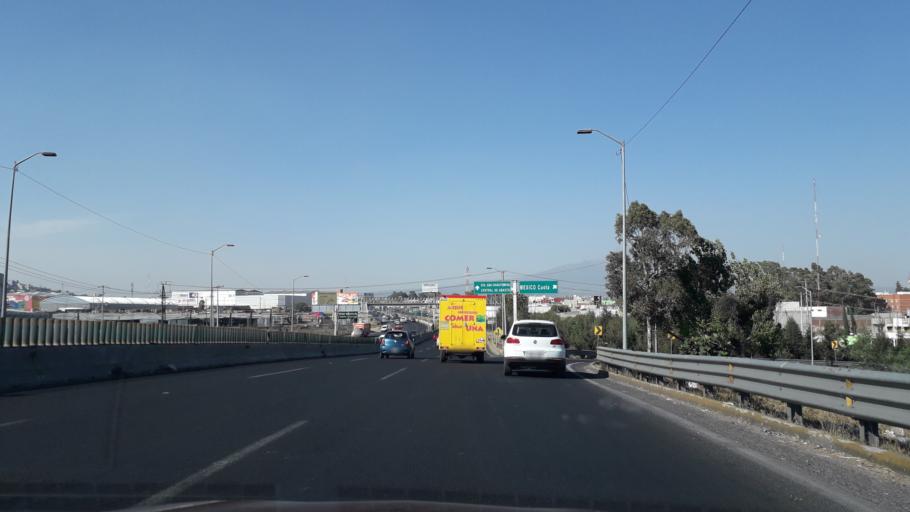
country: MX
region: Puebla
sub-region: Puebla
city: San Sebastian de Aparicio
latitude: 19.0848
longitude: -98.1877
